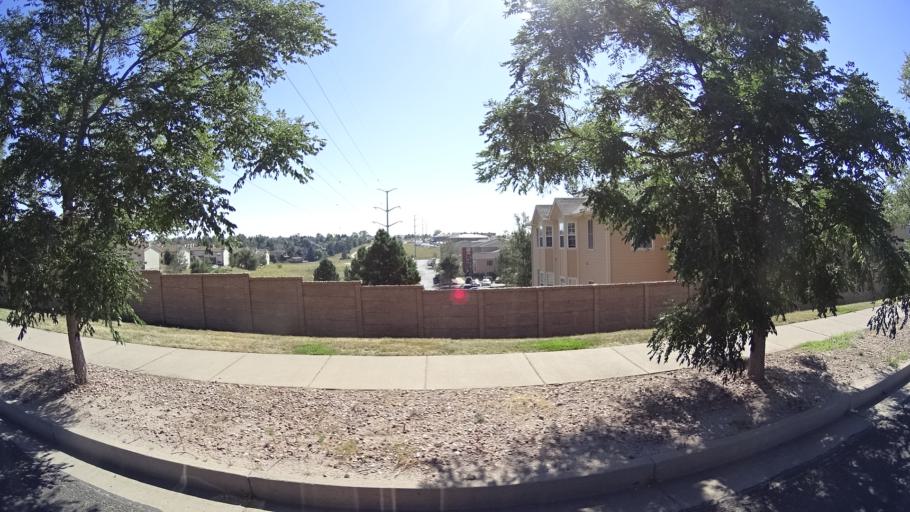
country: US
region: Colorado
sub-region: El Paso County
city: Black Forest
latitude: 38.9403
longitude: -104.7558
